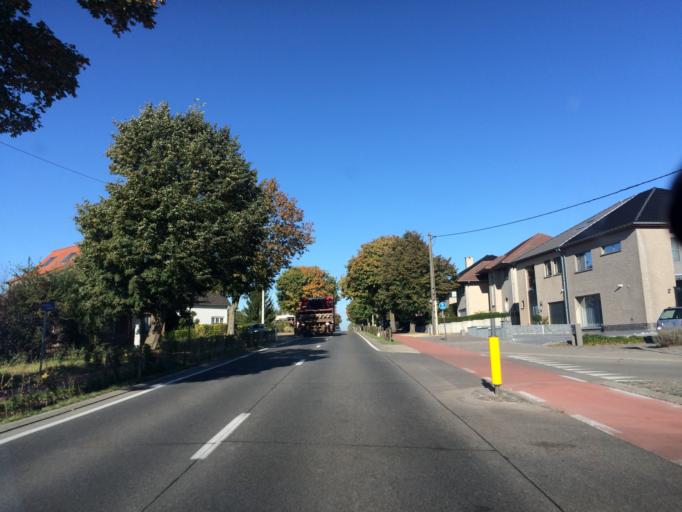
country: BE
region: Flanders
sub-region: Provincie Vlaams-Brabant
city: Merchtem
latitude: 50.9289
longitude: 4.2604
